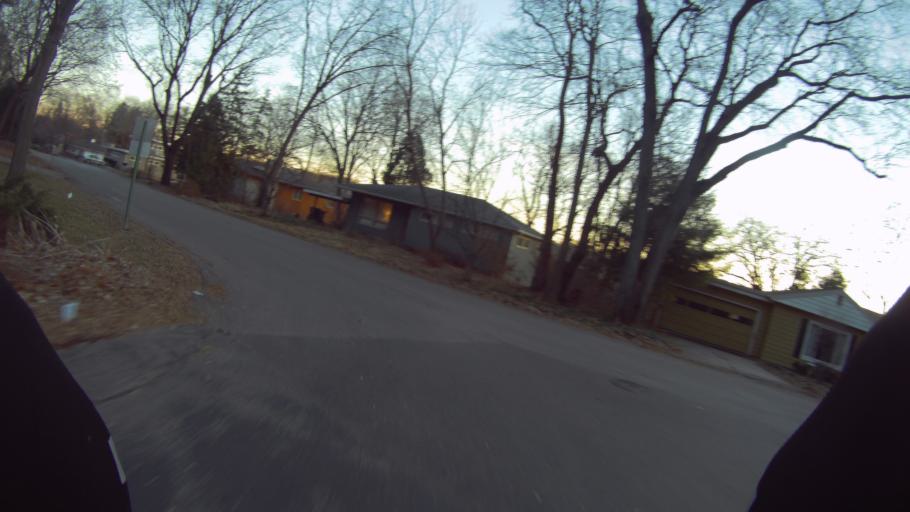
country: US
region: Wisconsin
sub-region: Dane County
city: Shorewood Hills
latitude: 43.0777
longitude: -89.4494
